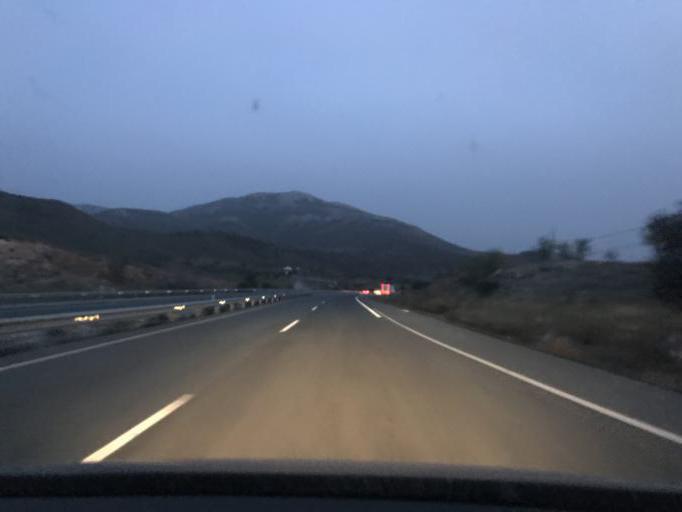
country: ES
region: Andalusia
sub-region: Provincia de Granada
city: Gor
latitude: 37.4129
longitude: -2.9191
